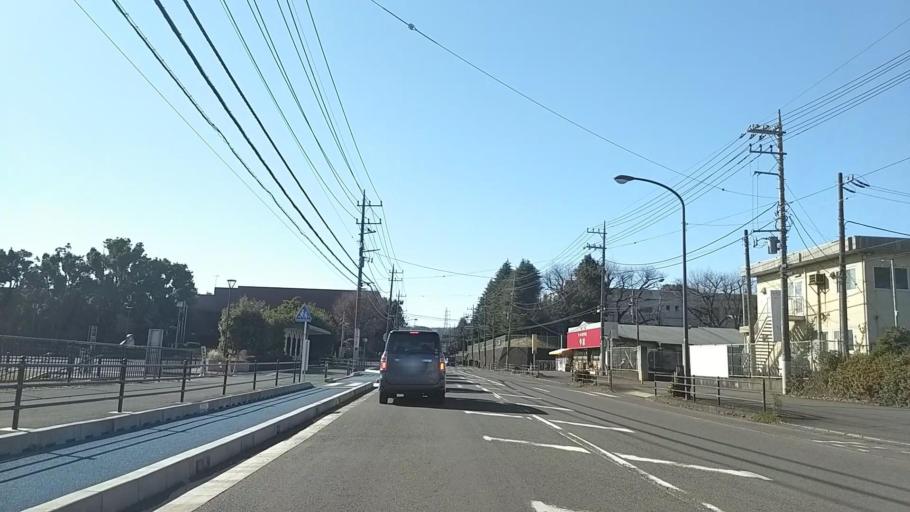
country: JP
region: Kanagawa
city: Hadano
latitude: 35.3819
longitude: 139.1979
